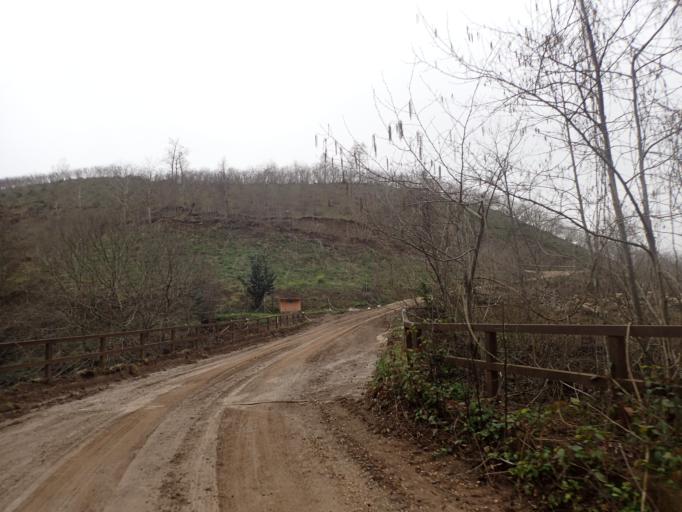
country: TR
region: Ordu
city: Camas
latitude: 40.9157
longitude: 37.5565
